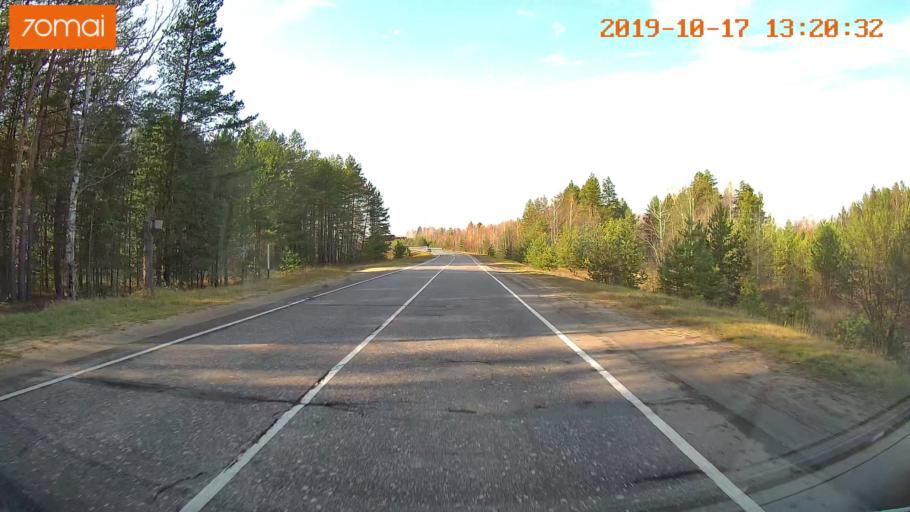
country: RU
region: Rjazan
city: Gus'-Zheleznyy
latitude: 55.0768
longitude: 41.0482
